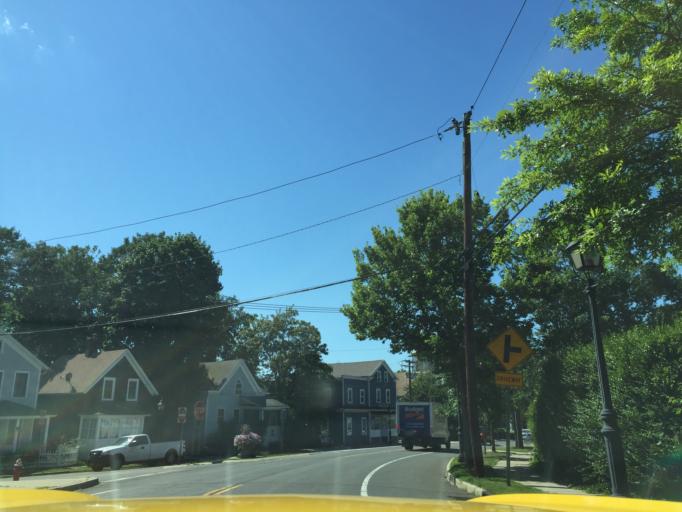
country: US
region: New York
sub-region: Suffolk County
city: Sag Harbor
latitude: 40.9979
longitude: -72.2919
